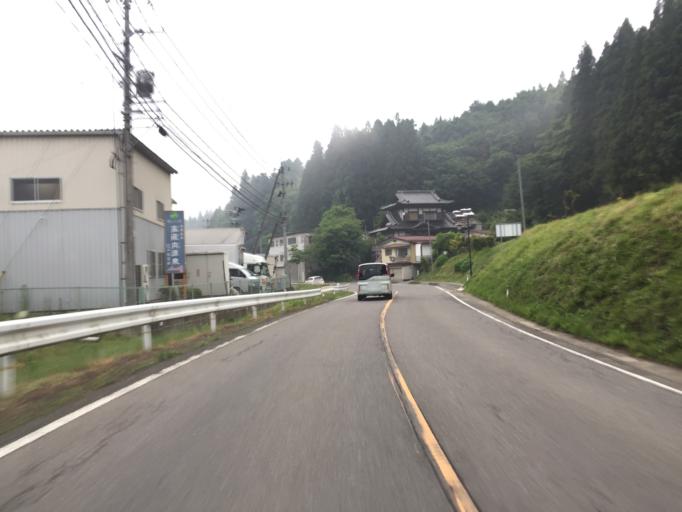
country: JP
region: Fukushima
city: Ishikawa
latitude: 37.1611
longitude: 140.4686
